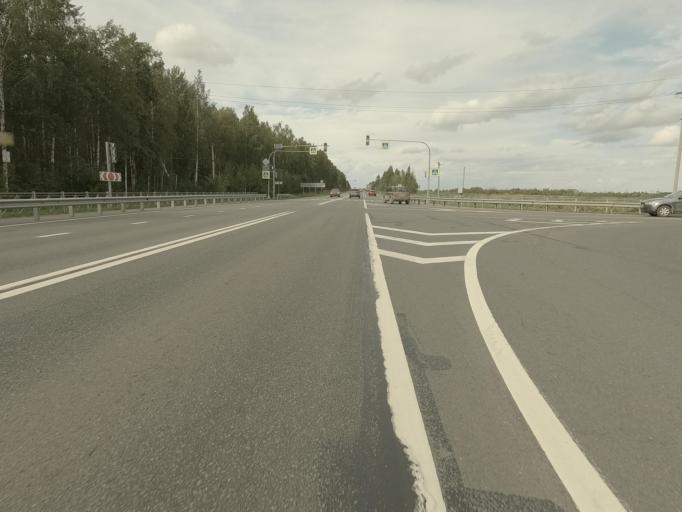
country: RU
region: Leningrad
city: Mga
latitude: 59.7843
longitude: 31.1053
